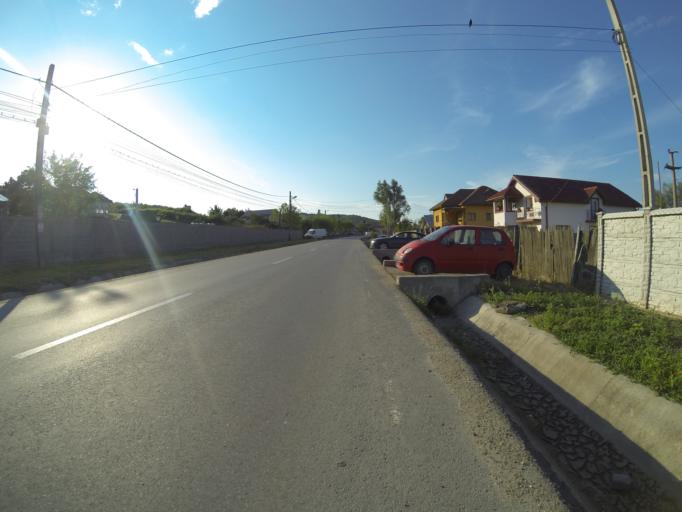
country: RO
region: Dolj
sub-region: Comuna Podari
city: Podari
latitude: 44.2241
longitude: 23.7896
